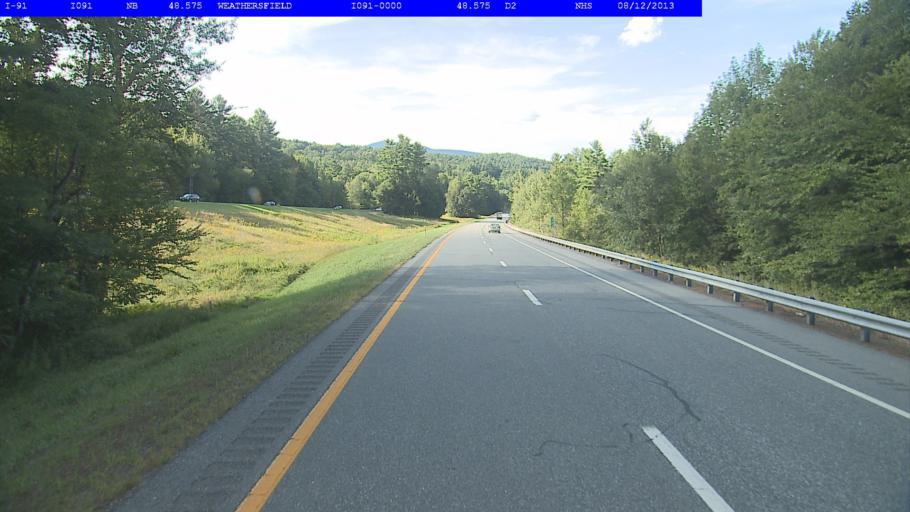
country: US
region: New Hampshire
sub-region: Sullivan County
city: Claremont
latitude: 43.3634
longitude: -72.4247
